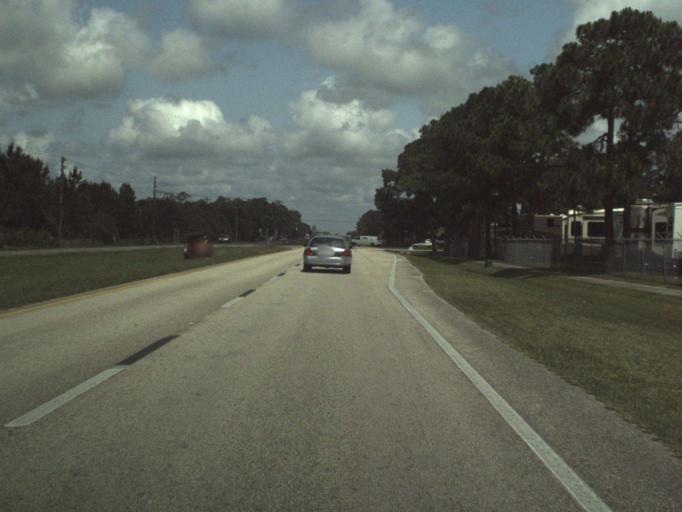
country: US
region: Florida
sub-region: Volusia County
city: Ormond-by-the-Sea
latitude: 29.3275
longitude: -81.1195
